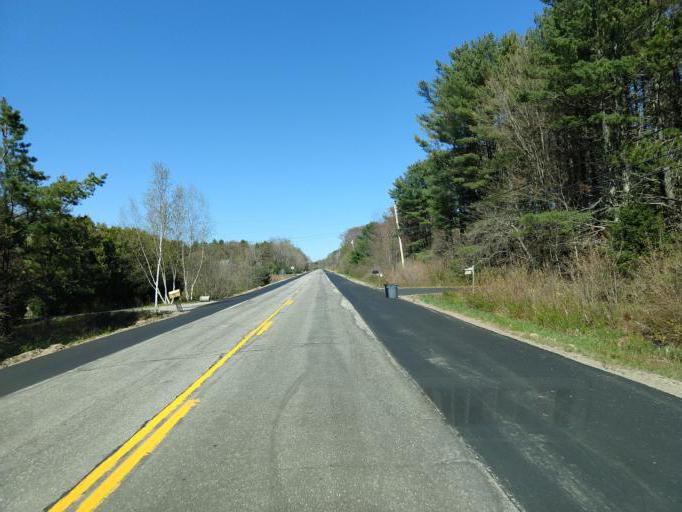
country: US
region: Maine
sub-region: York County
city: Arundel
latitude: 43.4141
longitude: -70.4137
